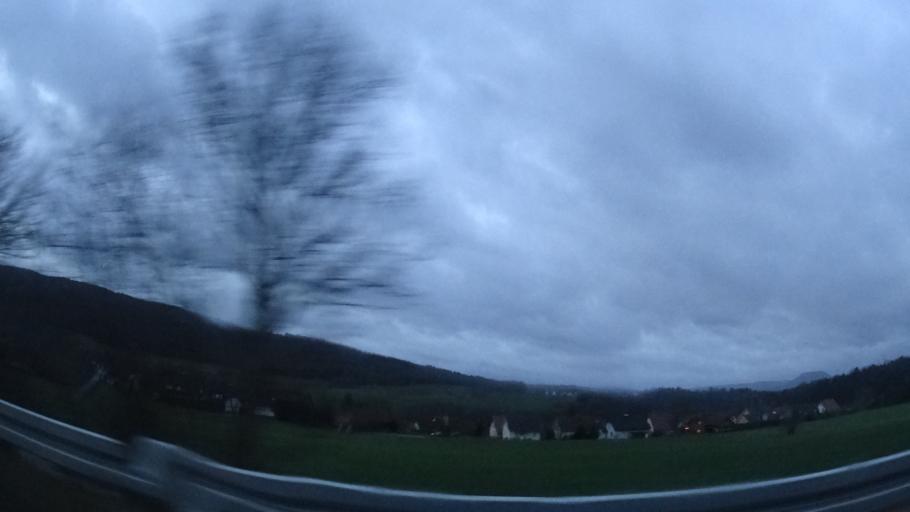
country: DE
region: Hesse
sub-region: Regierungsbezirk Kassel
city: Eichenzell
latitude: 50.4730
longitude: 9.6982
